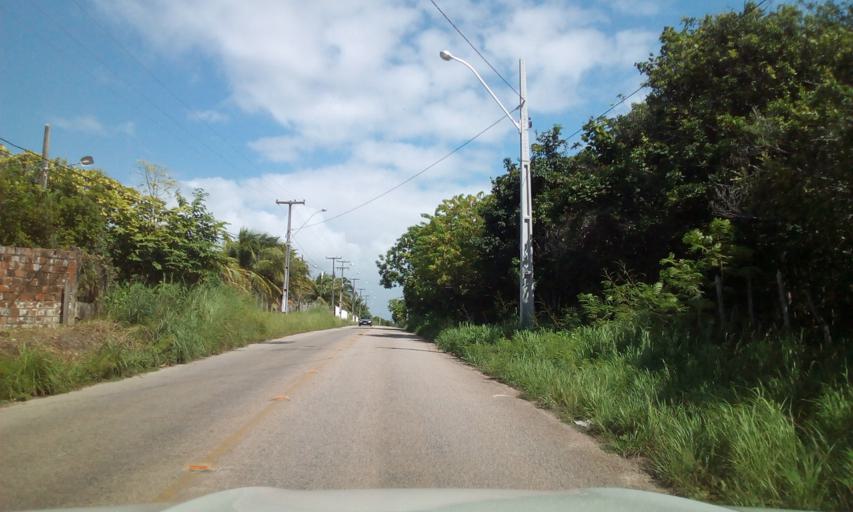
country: BR
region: Paraiba
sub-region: Conde
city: Conde
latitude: -7.2225
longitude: -34.8121
